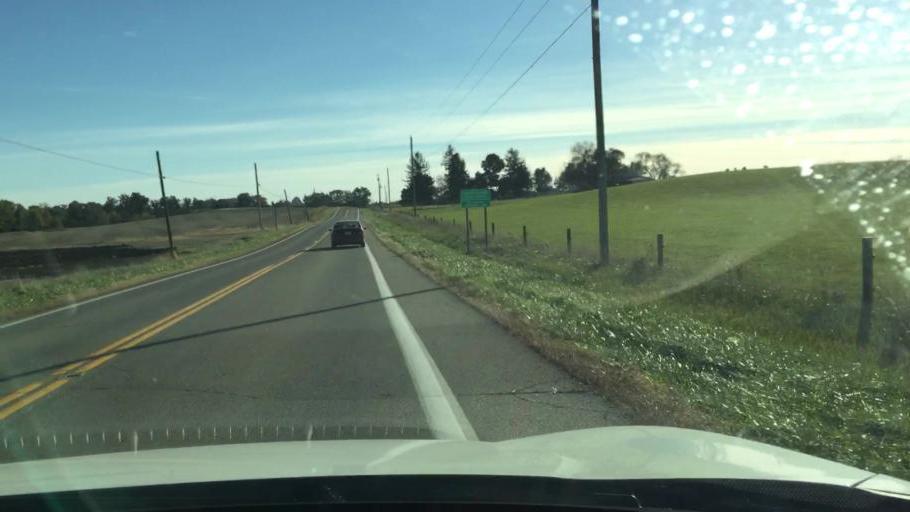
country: US
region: Ohio
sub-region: Champaign County
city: Mechanicsburg
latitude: 40.1003
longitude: -83.5436
